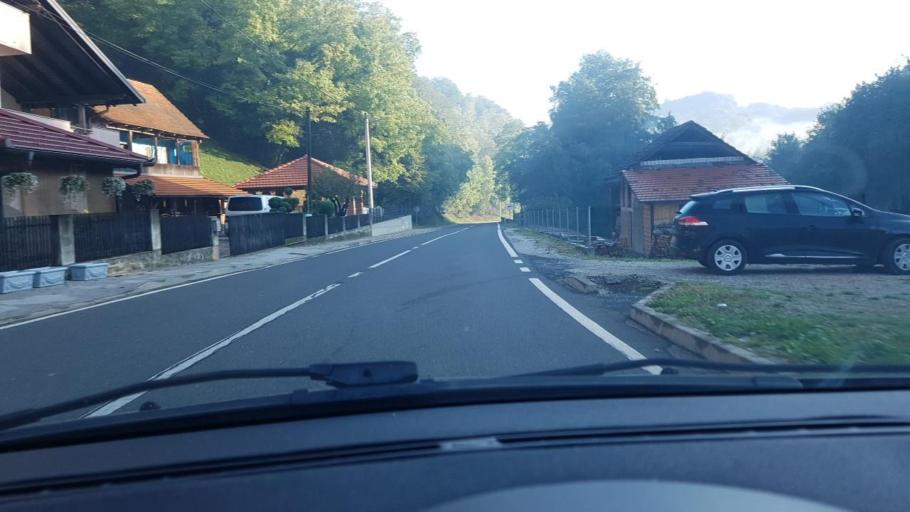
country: HR
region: Krapinsko-Zagorska
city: Marija Bistrica
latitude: 45.9818
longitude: 16.1099
